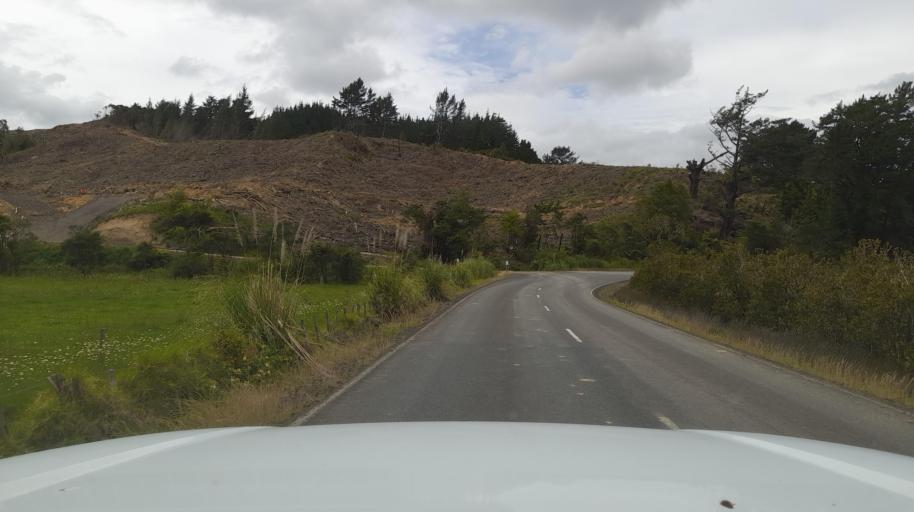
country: NZ
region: Northland
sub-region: Far North District
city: Kaitaia
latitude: -35.3613
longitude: 173.4456
